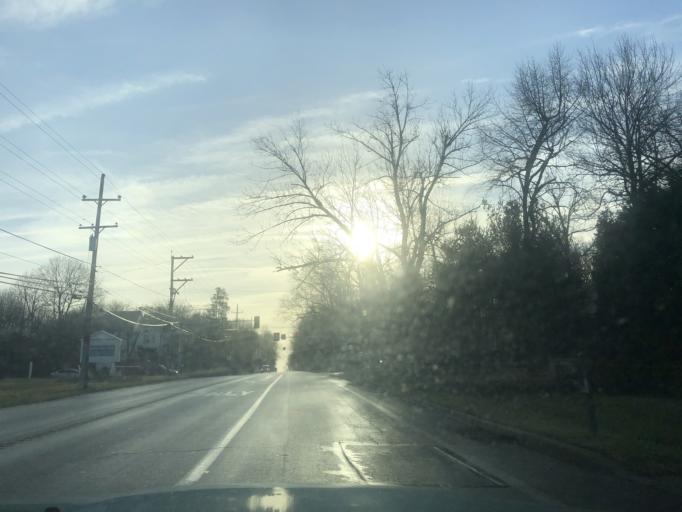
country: US
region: Pennsylvania
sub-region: Montgomery County
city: Dresher
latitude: 40.1368
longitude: -75.1601
